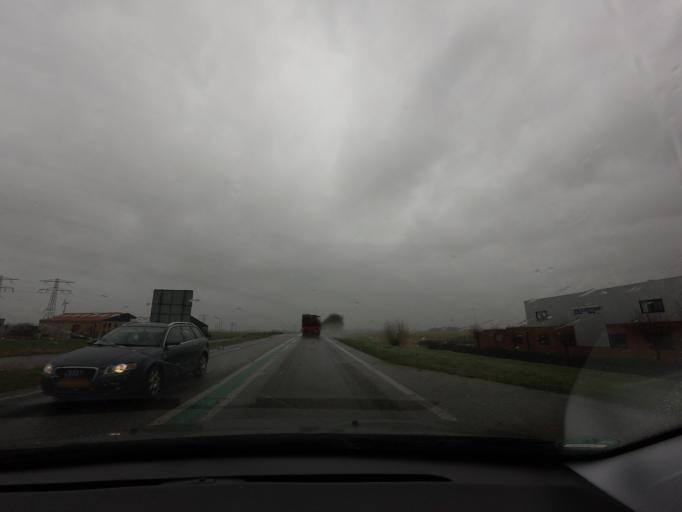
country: NL
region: Friesland
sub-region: Sudwest Fryslan
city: Bolsward
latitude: 53.0663
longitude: 5.5092
